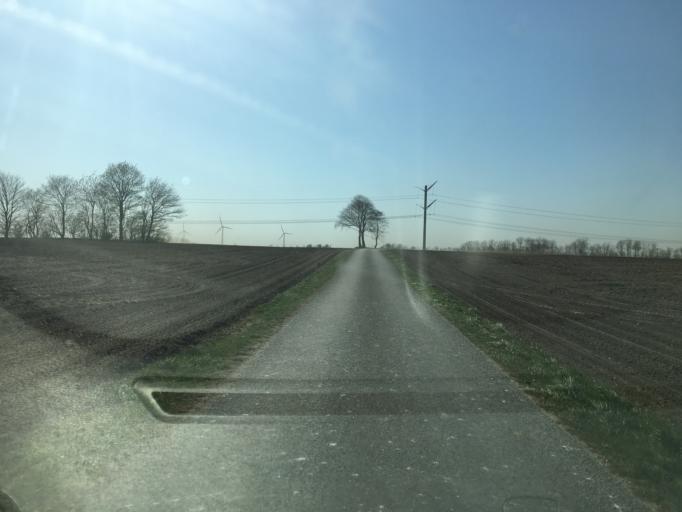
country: DK
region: South Denmark
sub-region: Aabenraa Kommune
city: Rodekro
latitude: 55.1098
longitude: 9.2187
